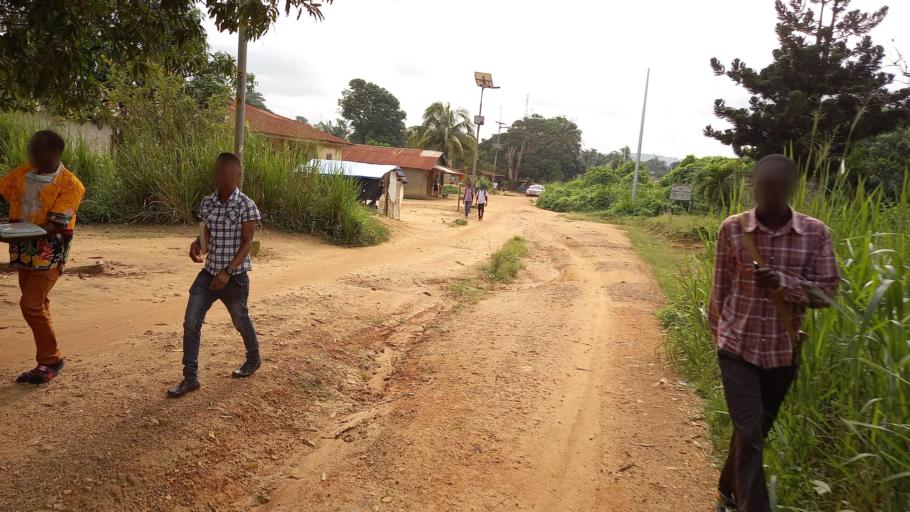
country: SL
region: Eastern Province
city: Kailahun
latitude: 8.2828
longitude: -10.5762
